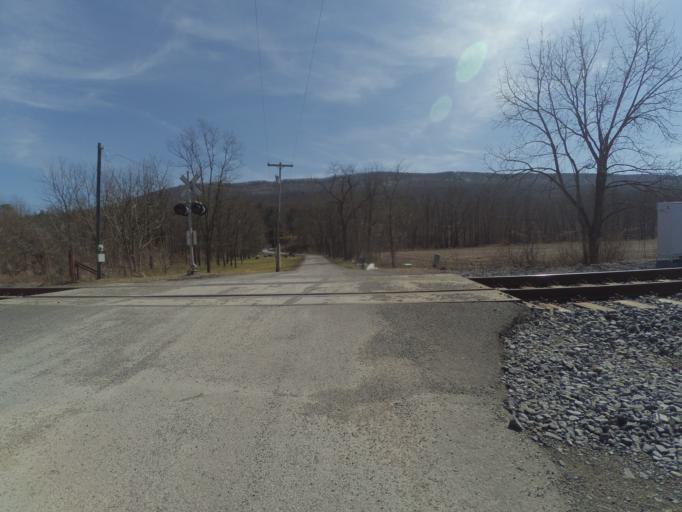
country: US
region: Pennsylvania
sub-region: Centre County
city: Milesburg
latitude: 40.9334
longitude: -77.8130
